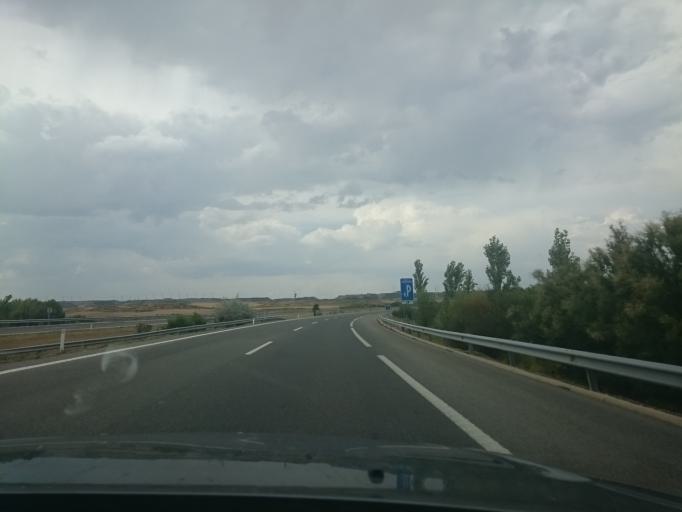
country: ES
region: Navarre
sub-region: Provincia de Navarra
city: Murchante
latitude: 42.0564
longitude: -1.6878
